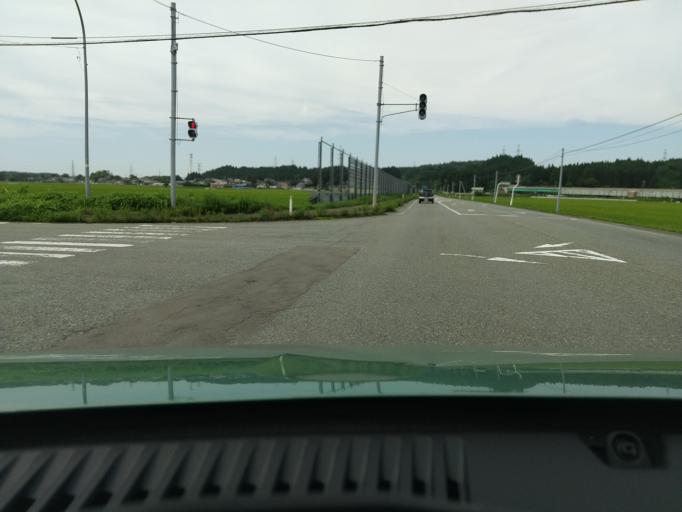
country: JP
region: Akita
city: Akita Shi
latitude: 39.8002
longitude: 140.0953
